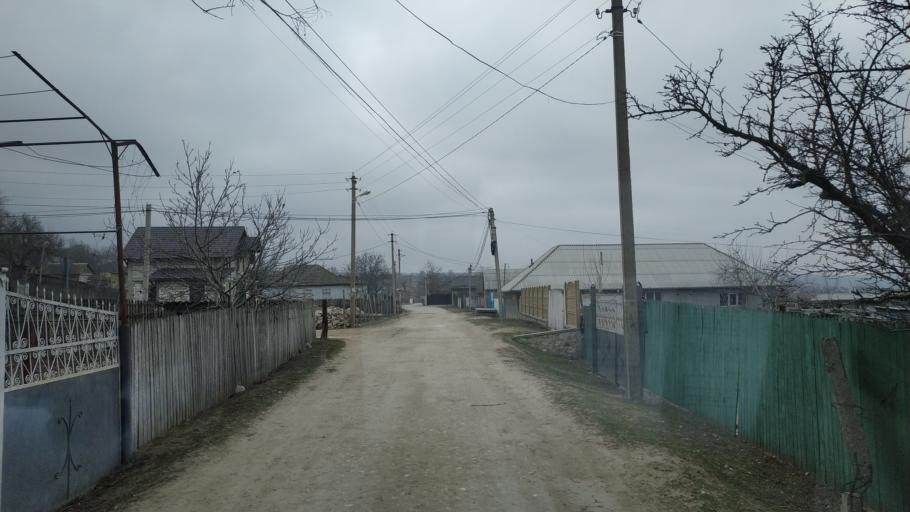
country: MD
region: Hincesti
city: Hincesti
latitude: 46.8865
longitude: 28.4052
